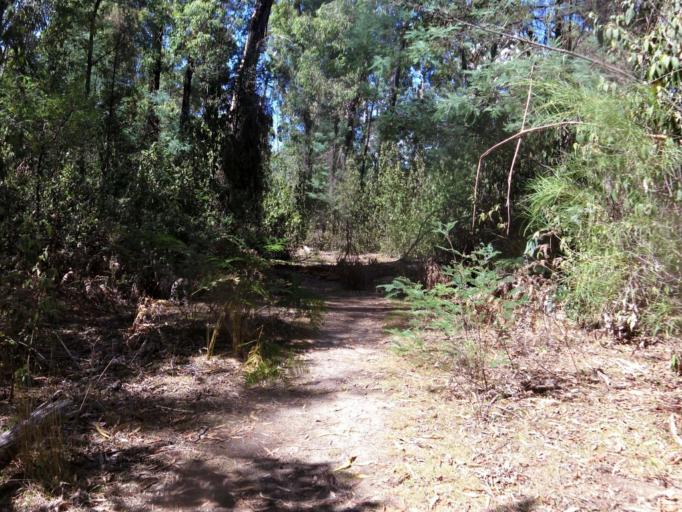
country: AU
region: Victoria
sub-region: Murrindindi
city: Alexandra
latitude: -37.3914
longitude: 145.5558
